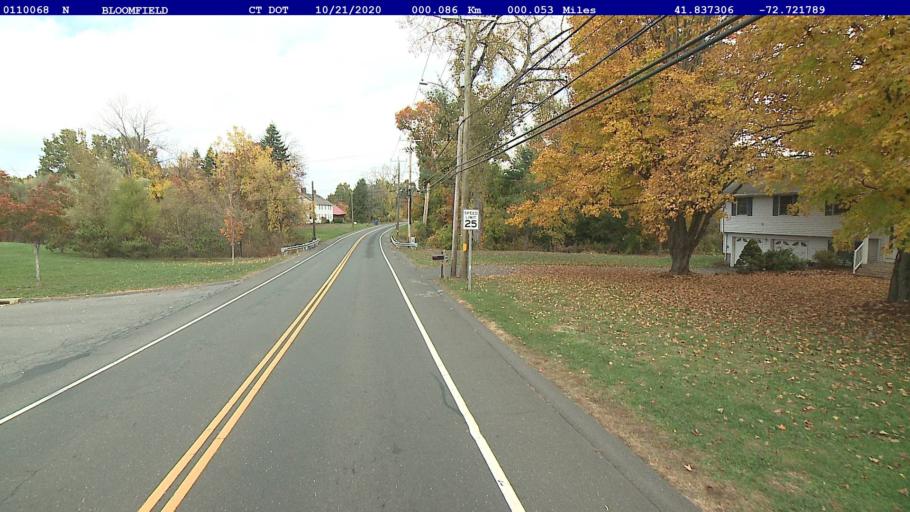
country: US
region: Connecticut
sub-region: Hartford County
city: Blue Hills
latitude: 41.8373
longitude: -72.7218
